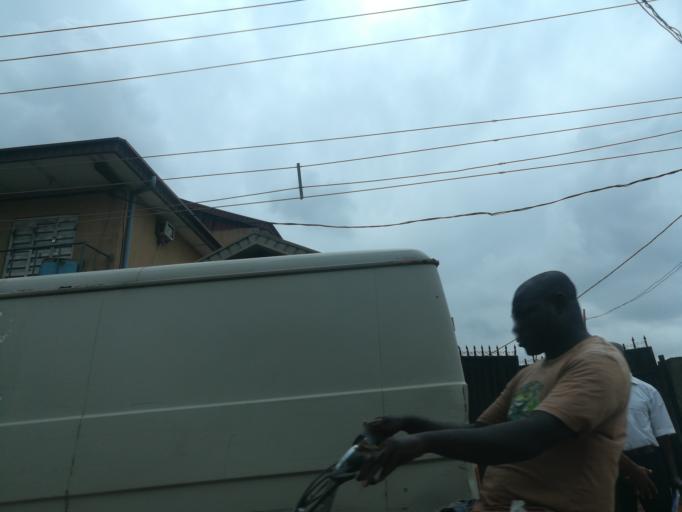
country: NG
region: Lagos
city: Ikeja
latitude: 6.5978
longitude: 3.3378
